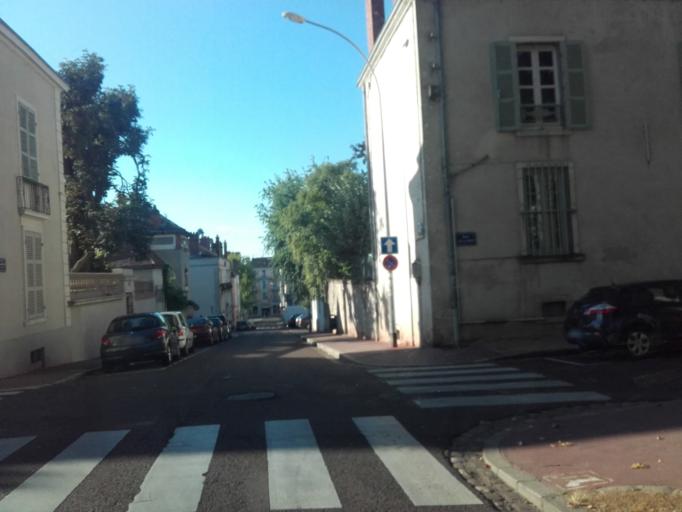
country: FR
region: Bourgogne
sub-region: Departement de Saone-et-Loire
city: Chalon-sur-Saone
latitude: 46.7856
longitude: 4.8502
